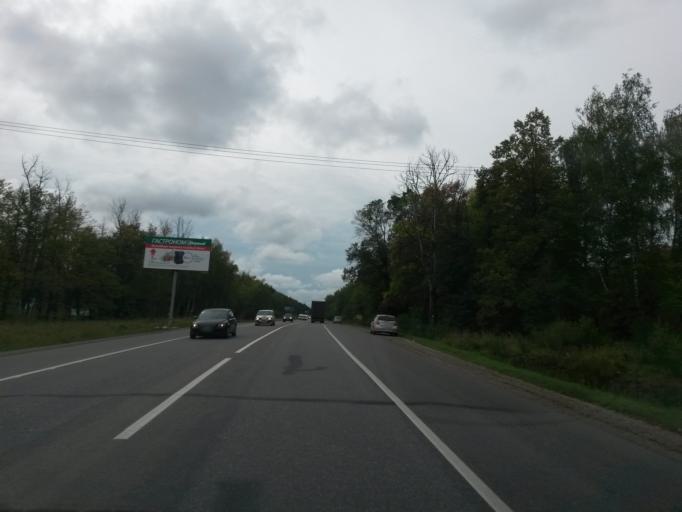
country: RU
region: Moskovskaya
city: Stolbovaya
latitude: 55.2008
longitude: 37.5065
